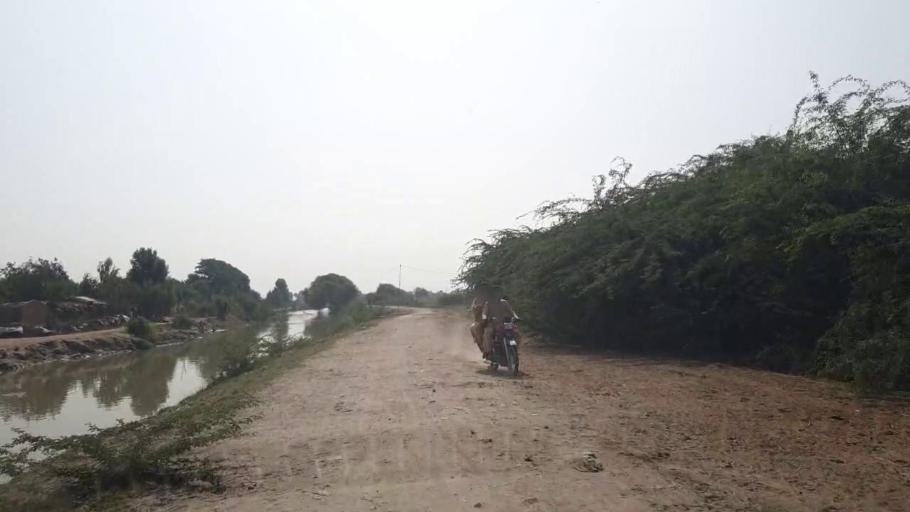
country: PK
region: Sindh
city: Badin
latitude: 24.6472
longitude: 68.8465
